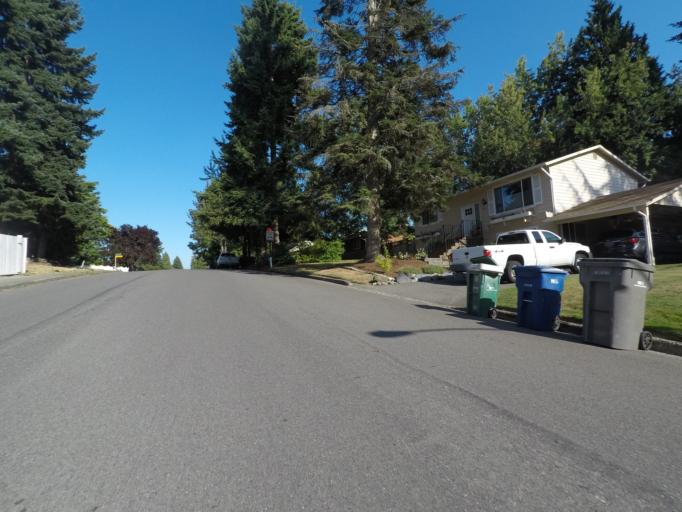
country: US
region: Washington
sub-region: King County
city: Inglewood-Finn Hill
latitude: 47.7334
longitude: -122.2372
